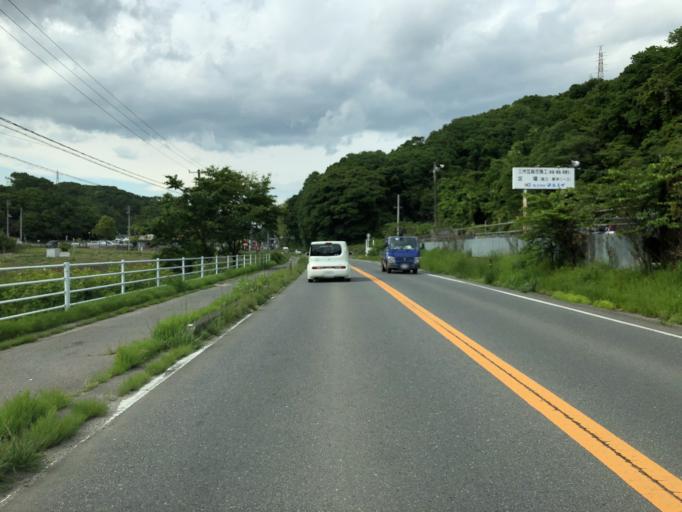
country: JP
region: Fukushima
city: Iwaki
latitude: 36.9630
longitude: 140.8718
